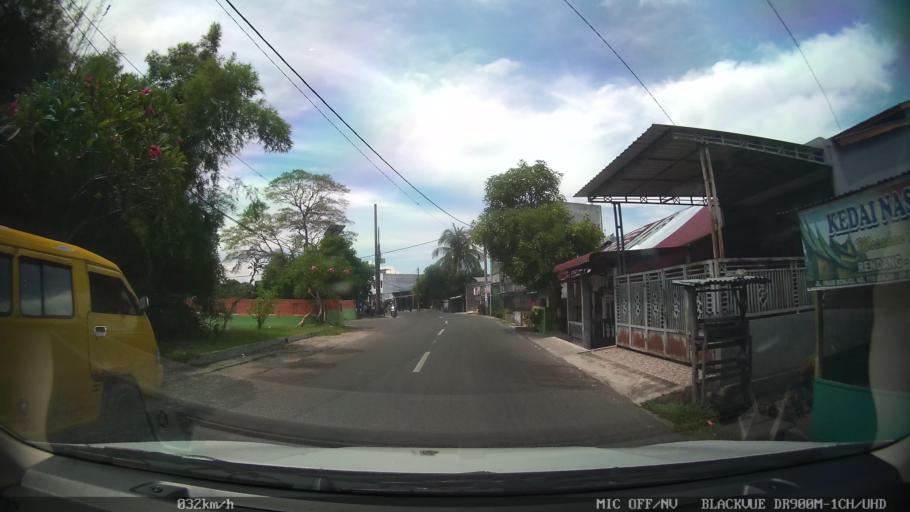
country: ID
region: North Sumatra
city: Binjai
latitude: 3.6046
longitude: 98.4896
